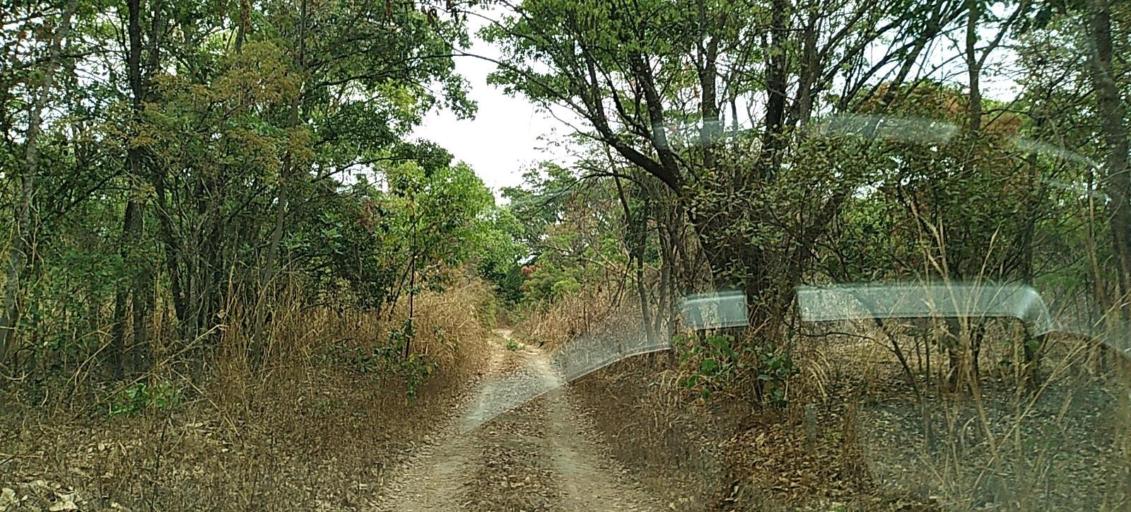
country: ZM
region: Copperbelt
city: Chililabombwe
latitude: -12.3286
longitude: 27.7703
